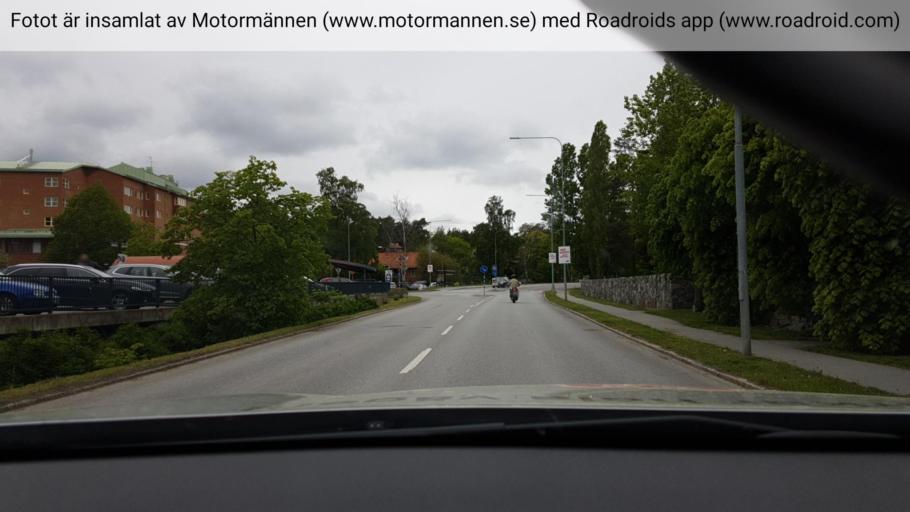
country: SE
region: Stockholm
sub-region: Lidingo
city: Lidingoe
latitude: 59.3667
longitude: 18.1355
